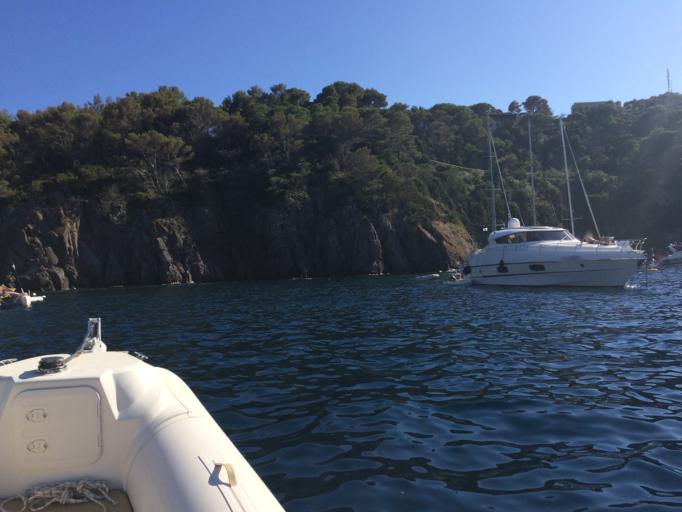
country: IT
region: Tuscany
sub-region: Provincia di Livorno
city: Capraia Isola
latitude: 43.0502
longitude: 9.8402
